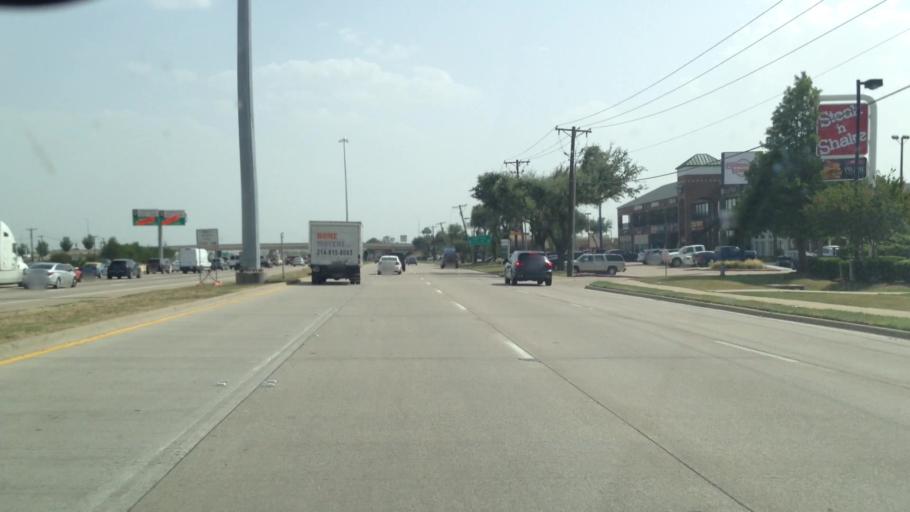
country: US
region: Texas
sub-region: Collin County
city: Plano
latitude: 33.0319
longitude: -96.7079
